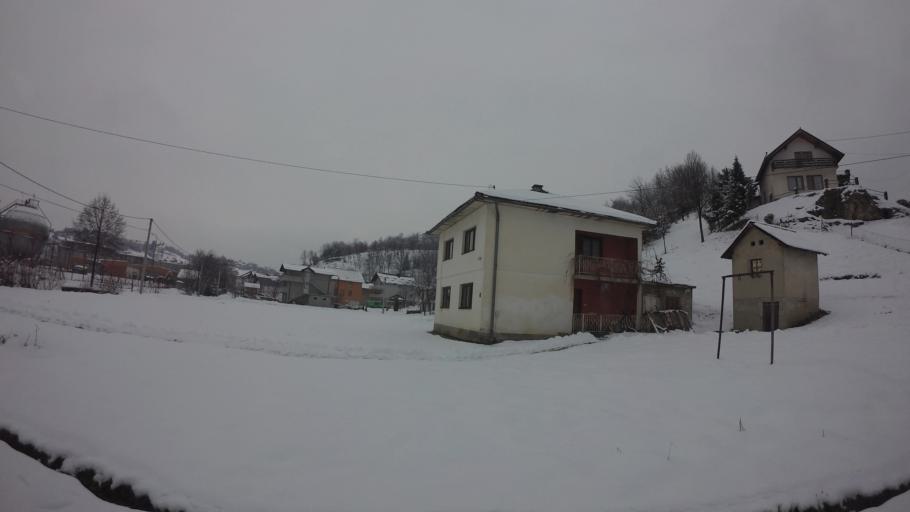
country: BA
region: Federation of Bosnia and Herzegovina
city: Hadzici
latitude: 43.8493
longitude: 18.2529
